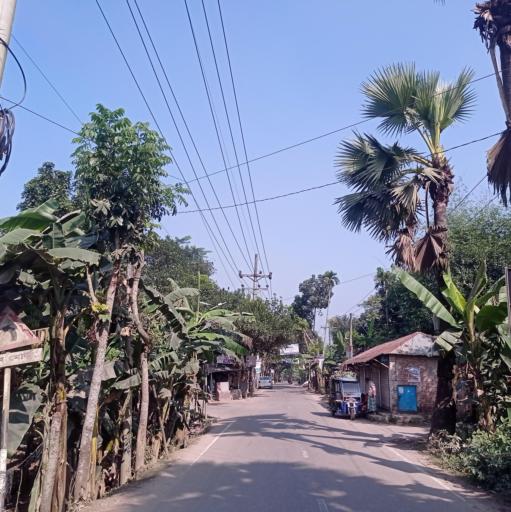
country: BD
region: Dhaka
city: Narsingdi
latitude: 24.0252
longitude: 90.6699
